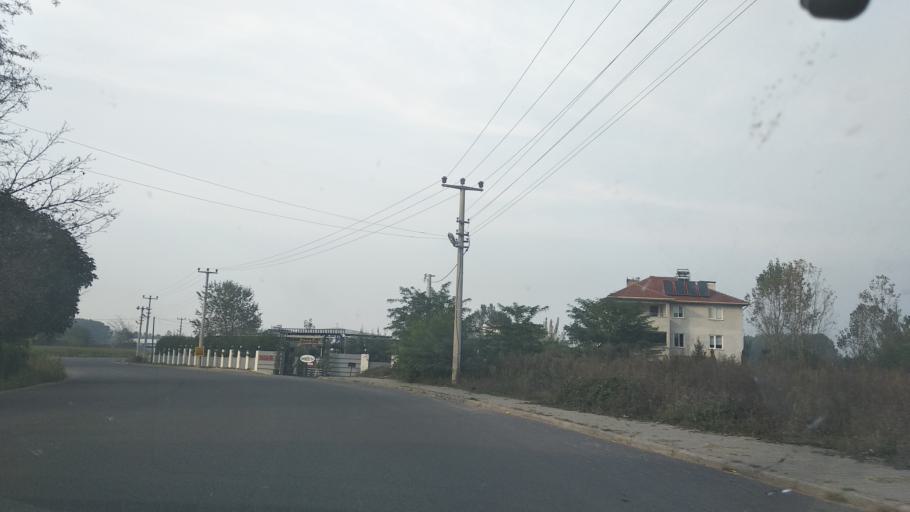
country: TR
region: Duzce
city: Duzce
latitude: 40.8102
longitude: 31.1785
